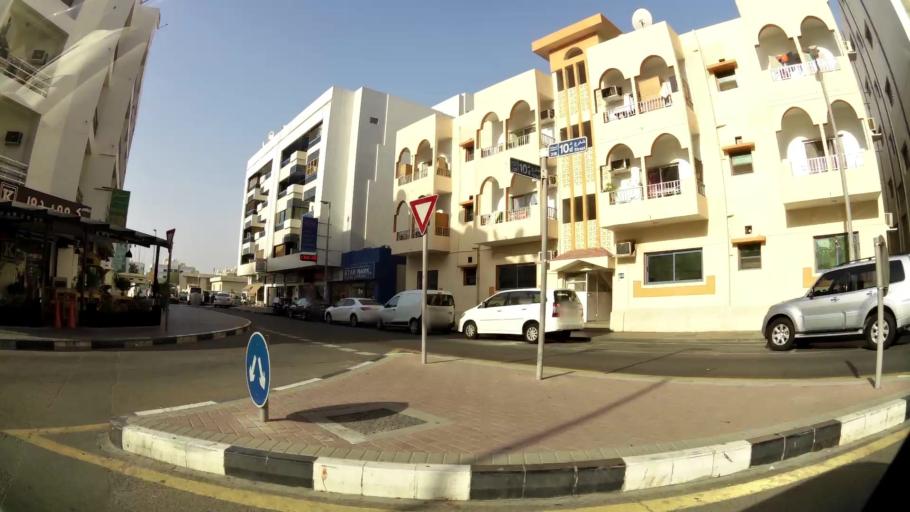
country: AE
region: Ash Shariqah
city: Sharjah
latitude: 25.2459
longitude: 55.3037
